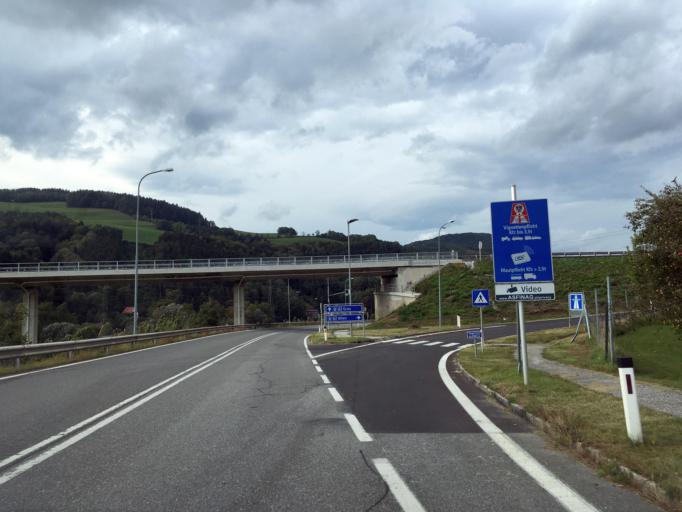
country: AT
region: Lower Austria
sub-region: Politischer Bezirk Neunkirchen
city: Grimmenstein
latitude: 47.6086
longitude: 16.1257
